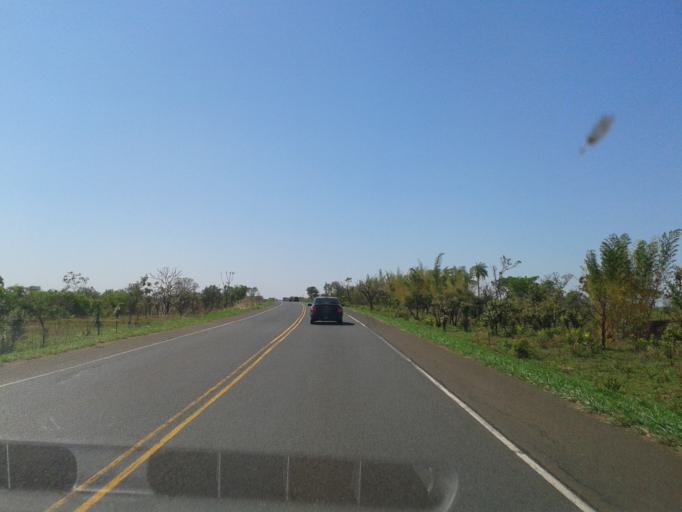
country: BR
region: Minas Gerais
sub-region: Uberlandia
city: Uberlandia
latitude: -19.0364
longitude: -48.0631
